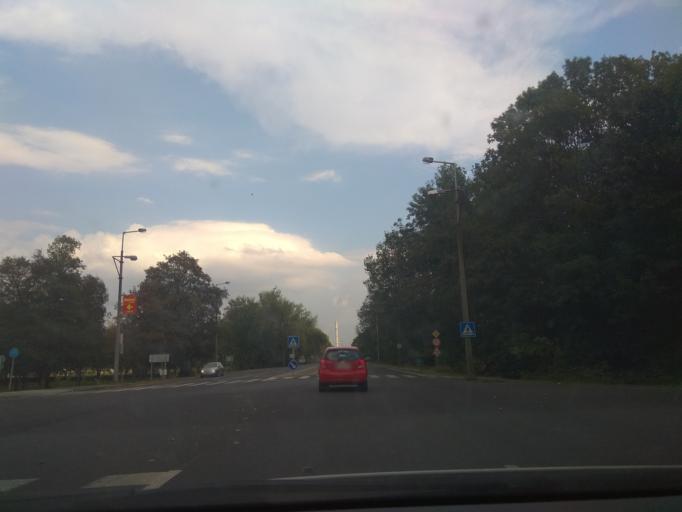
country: HU
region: Borsod-Abauj-Zemplen
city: Sajooeroes
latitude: 47.9284
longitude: 21.0316
